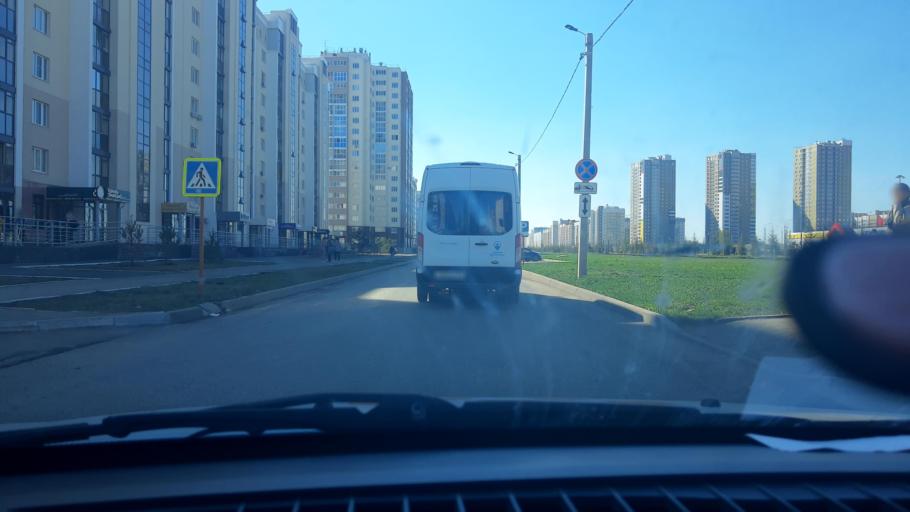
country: RU
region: Bashkortostan
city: Sterlitamak
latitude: 53.6292
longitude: 55.9032
